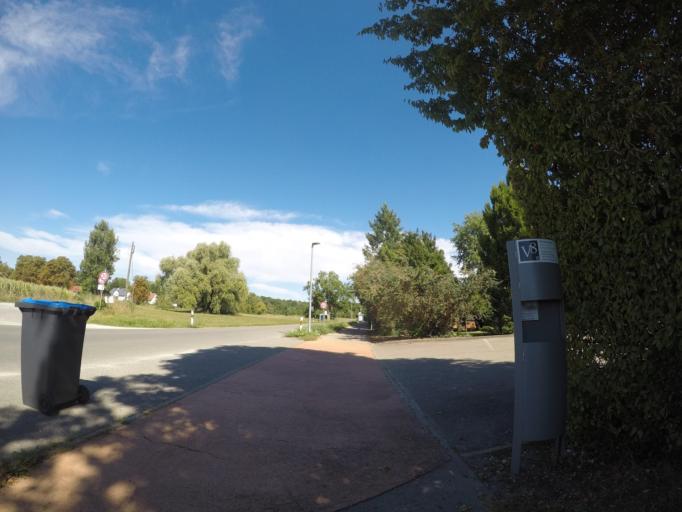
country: DE
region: Bavaria
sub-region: Swabia
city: Senden
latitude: 48.3336
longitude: 10.0233
